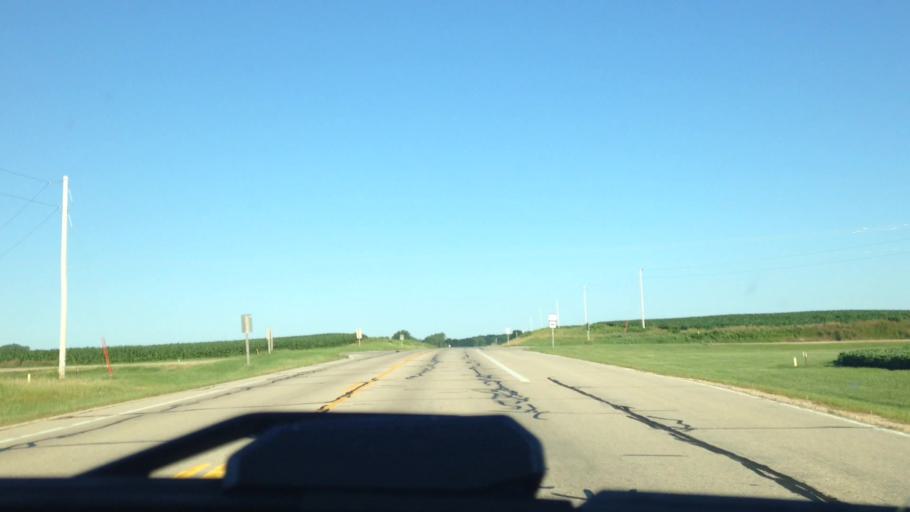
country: US
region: Wisconsin
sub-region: Columbia County
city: Rio
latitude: 43.3403
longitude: -89.2435
